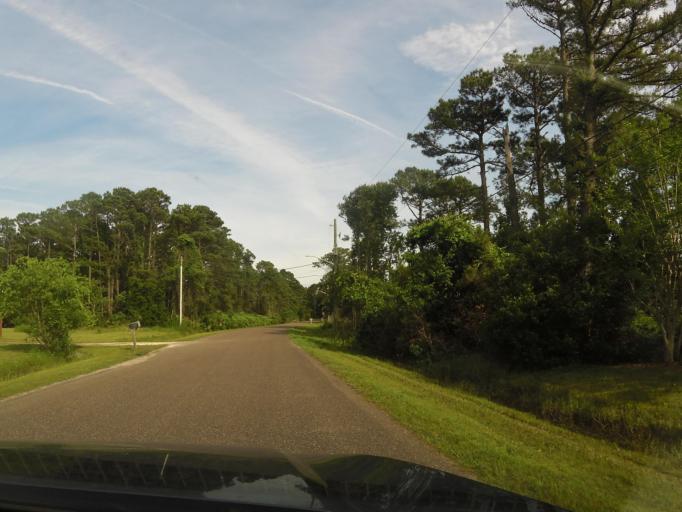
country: US
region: Florida
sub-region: Nassau County
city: Fernandina Beach
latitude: 30.5113
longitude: -81.4817
